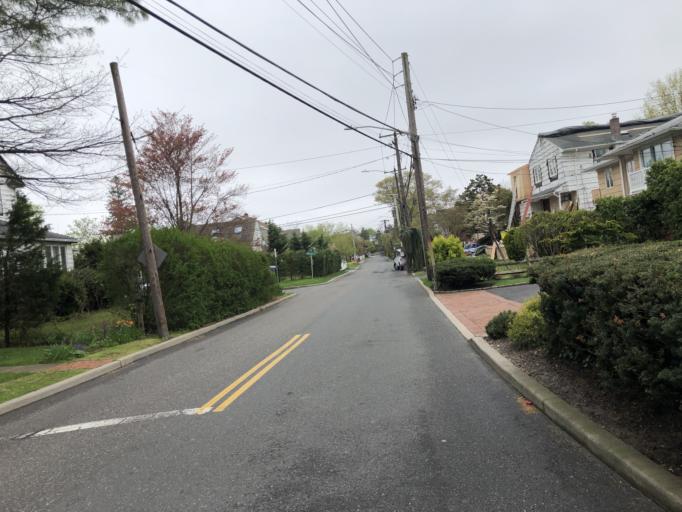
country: US
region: New York
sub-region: Nassau County
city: Woodmere
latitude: 40.6310
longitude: -73.7024
